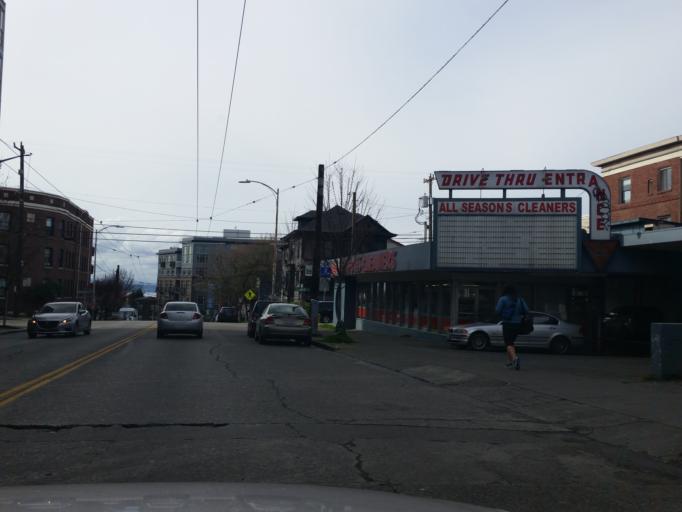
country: US
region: Washington
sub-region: King County
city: Seattle
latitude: 47.6199
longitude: -122.3214
